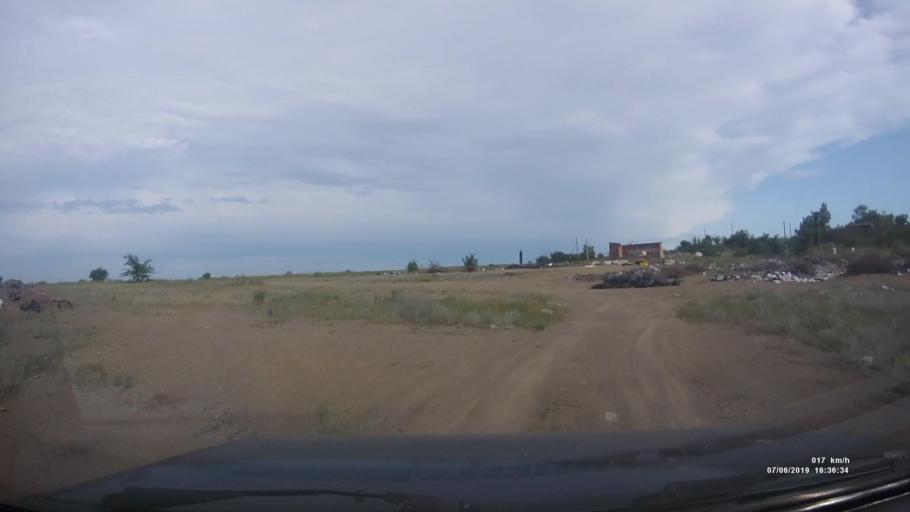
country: RU
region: Rostov
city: Staraya Stanitsa
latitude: 48.2528
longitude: 40.3520
